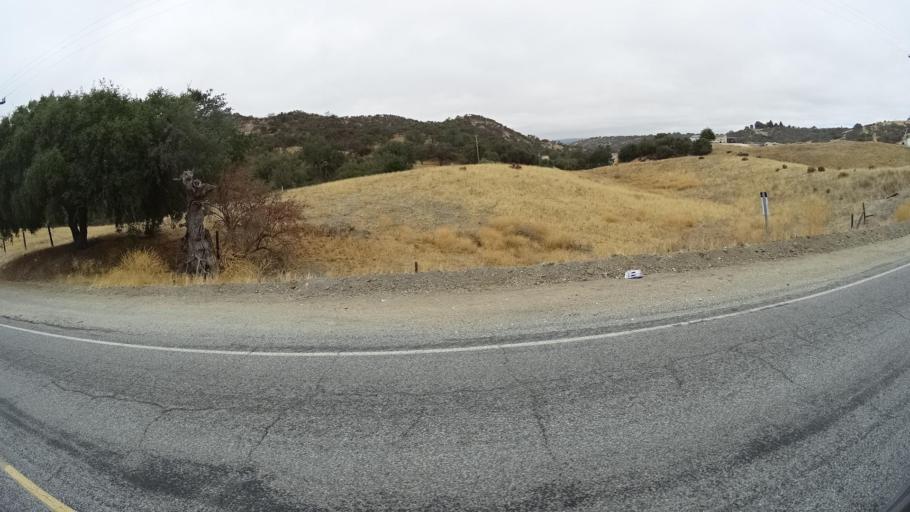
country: US
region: California
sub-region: San Luis Obispo County
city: Lake Nacimiento
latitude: 35.9047
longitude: -120.9806
